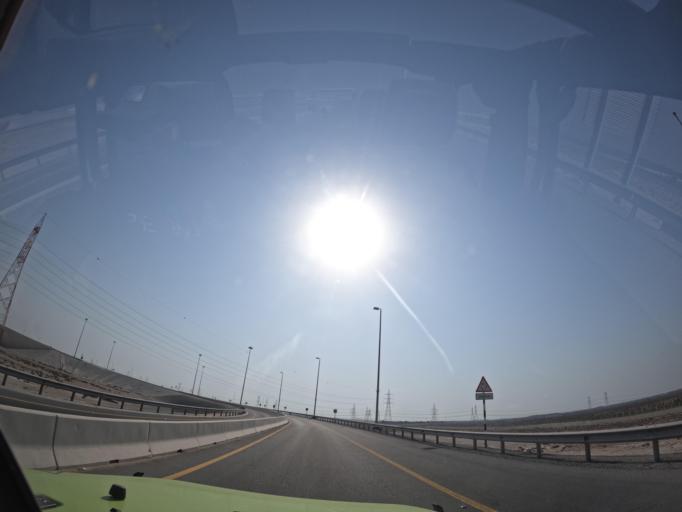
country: AE
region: Abu Dhabi
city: Abu Dhabi
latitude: 24.6173
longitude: 54.7623
